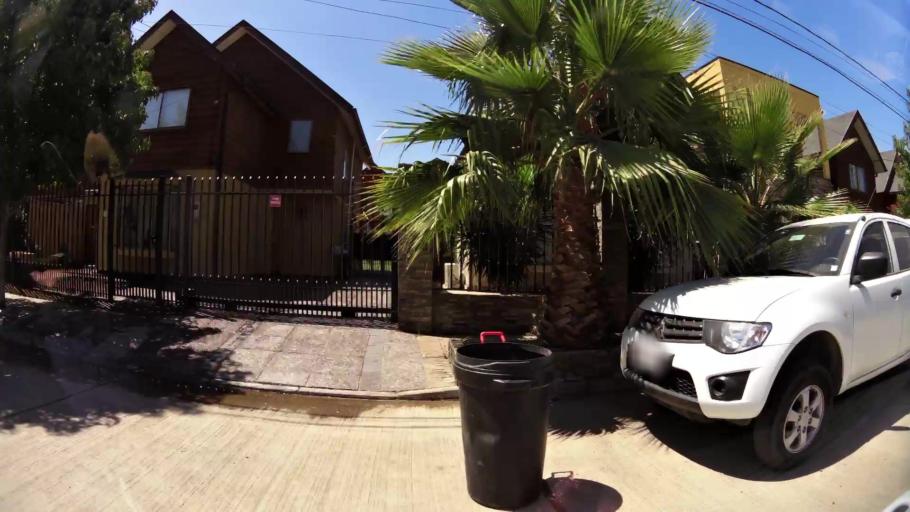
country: CL
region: Maule
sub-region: Provincia de Talca
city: Talca
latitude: -35.4263
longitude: -71.6117
